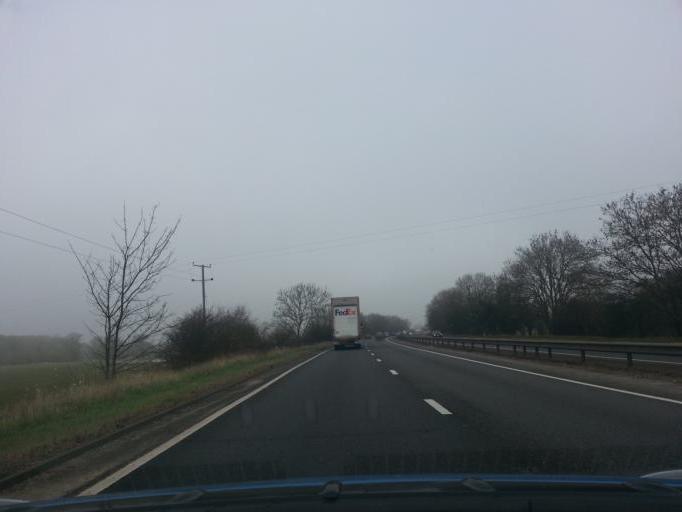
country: GB
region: England
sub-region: Oxfordshire
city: Yarnton
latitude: 51.7709
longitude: -1.3034
